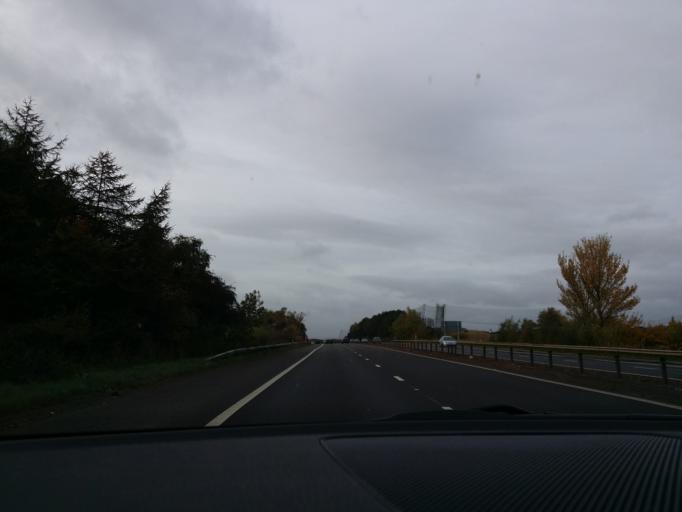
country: GB
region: Scotland
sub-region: Falkirk
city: Polmont
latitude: 55.9868
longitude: -3.6647
